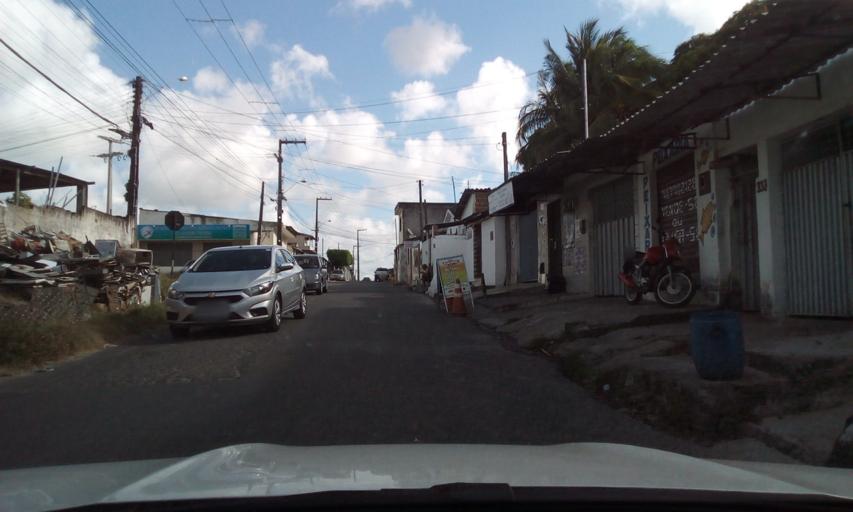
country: BR
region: Paraiba
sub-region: Bayeux
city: Bayeux
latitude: -7.1737
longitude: -34.8950
